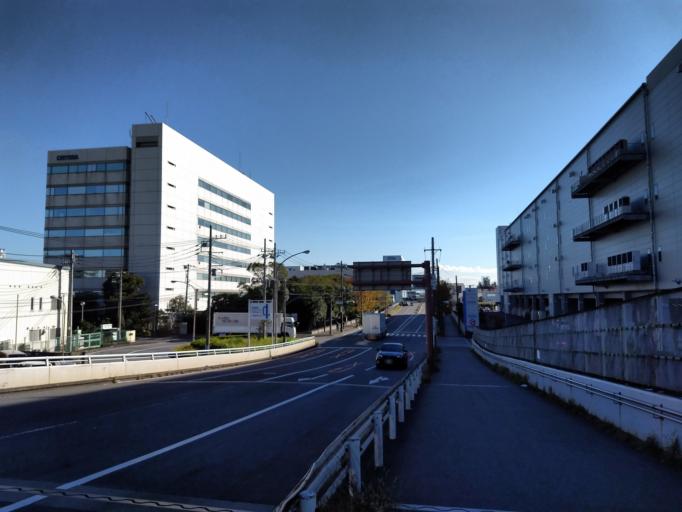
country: JP
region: Kanagawa
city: Yokohama
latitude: 35.4849
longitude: 139.6555
